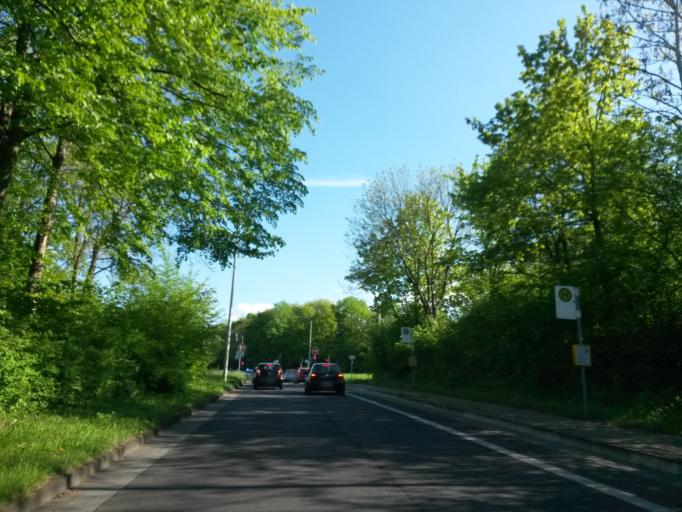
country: DE
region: North Rhine-Westphalia
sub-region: Regierungsbezirk Koln
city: Bonn
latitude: 50.7047
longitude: 7.0581
